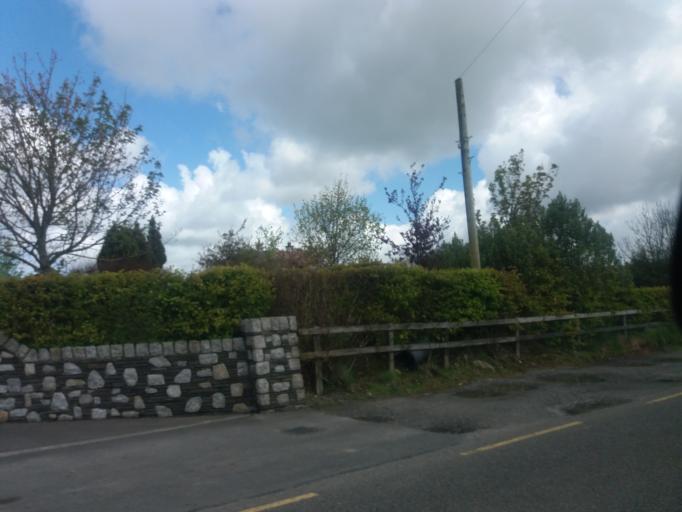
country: IE
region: Leinster
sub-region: Loch Garman
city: Loch Garman
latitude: 52.3089
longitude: -6.5478
